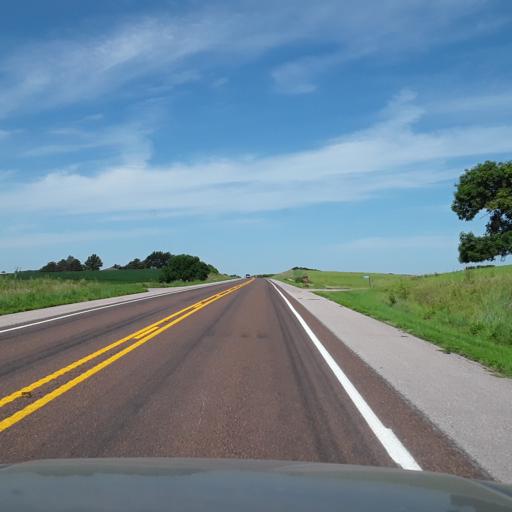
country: US
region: Nebraska
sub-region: Lancaster County
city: Lincoln
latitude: 40.8868
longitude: -96.8486
